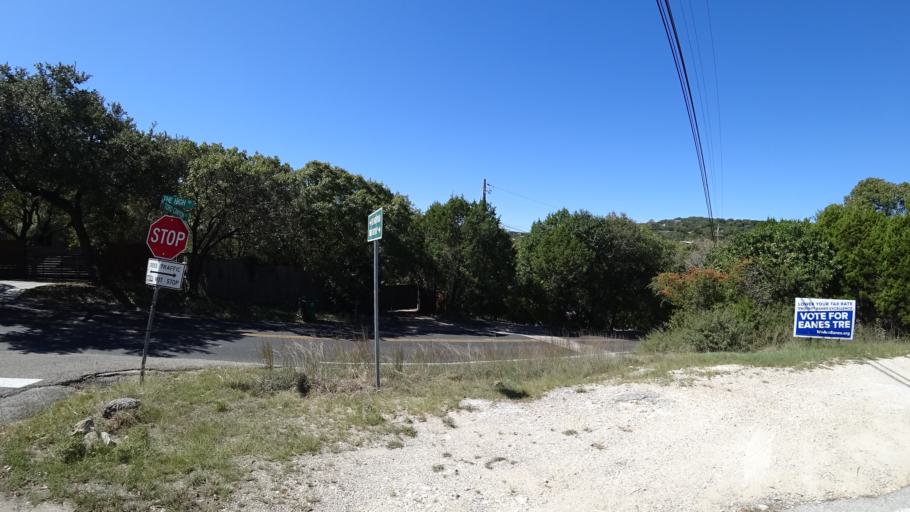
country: US
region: Texas
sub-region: Travis County
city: West Lake Hills
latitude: 30.3085
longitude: -97.7973
